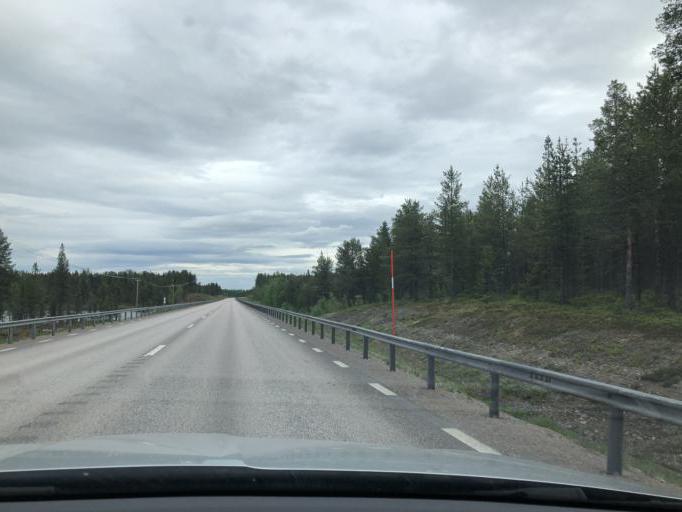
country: SE
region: Norrbotten
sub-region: Gallivare Kommun
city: Malmberget
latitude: 67.6413
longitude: 21.0971
